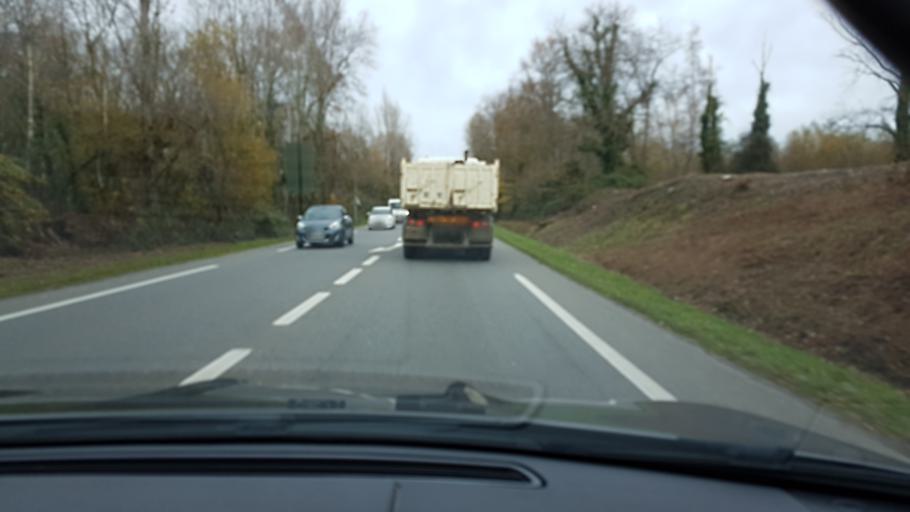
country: FR
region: Aquitaine
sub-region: Departement des Pyrenees-Atlantiques
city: Idron
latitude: 43.3087
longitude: -0.3067
